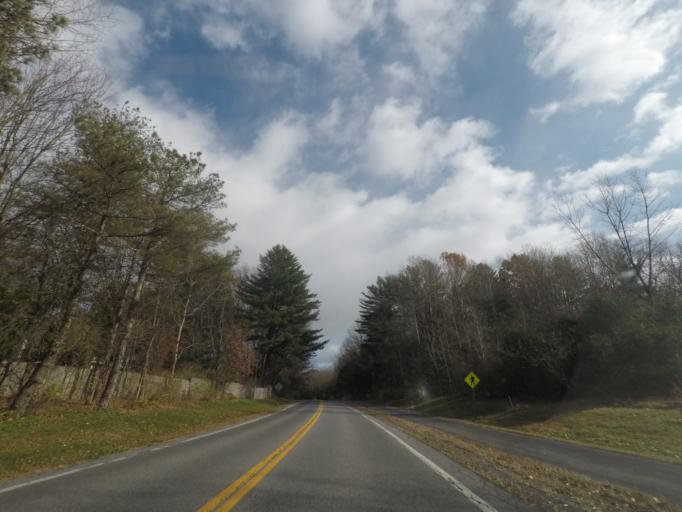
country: US
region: New York
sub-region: Saratoga County
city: Country Knolls
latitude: 42.8931
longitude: -73.8090
